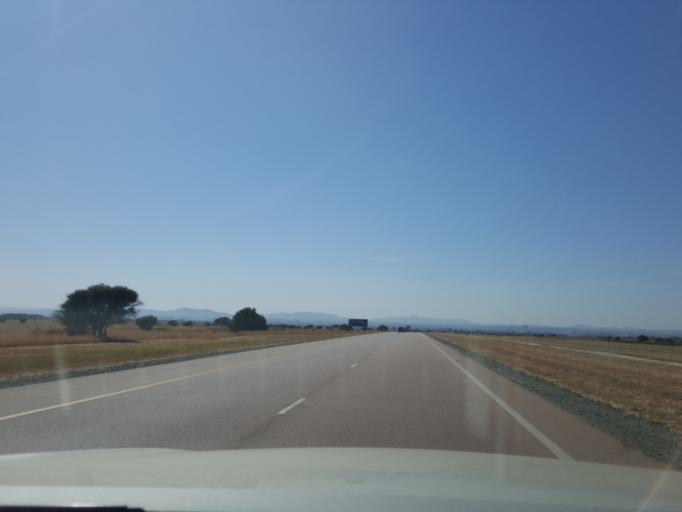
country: ZA
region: North-West
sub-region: Bojanala Platinum District Municipality
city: Brits
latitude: -25.6984
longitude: 27.7270
